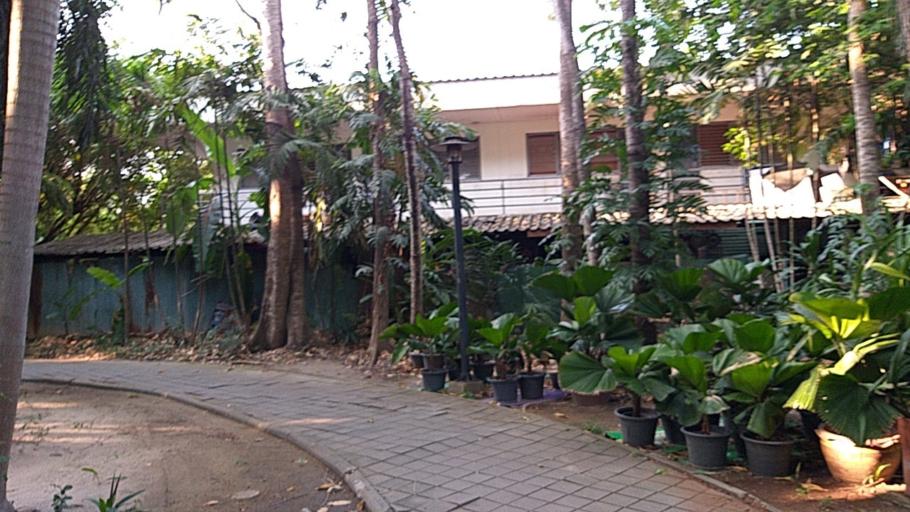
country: TH
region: Bangkok
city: Don Mueang
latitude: 13.9325
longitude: 100.5555
